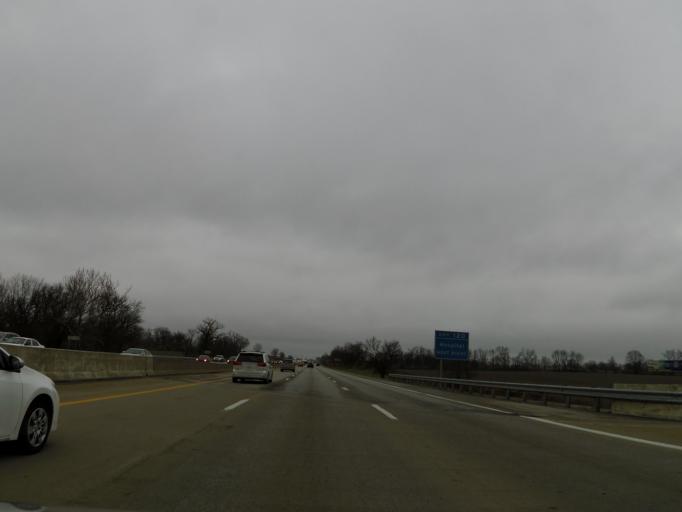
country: US
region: Kentucky
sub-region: Scott County
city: Georgetown
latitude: 38.1655
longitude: -84.5365
